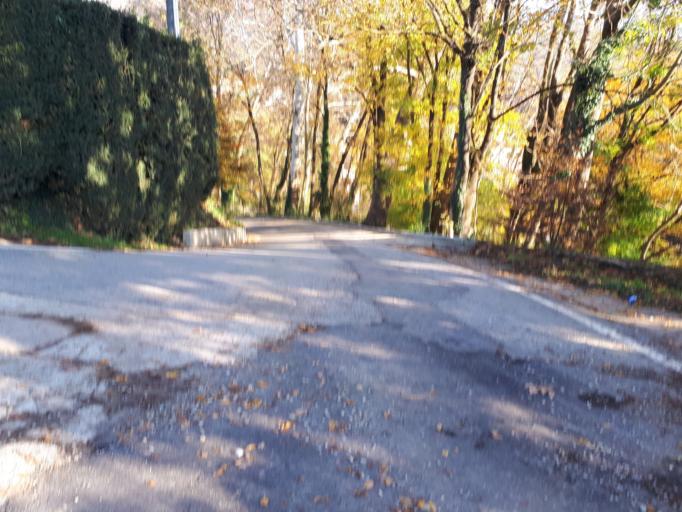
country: IT
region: Lombardy
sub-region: Provincia di Lecco
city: Maresso
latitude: 45.7003
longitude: 9.3583
